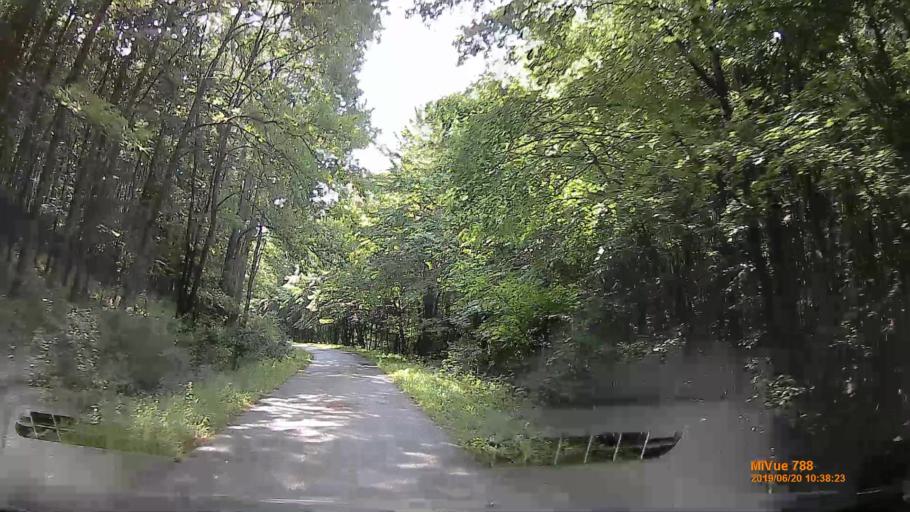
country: HU
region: Baranya
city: Hidas
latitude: 46.2004
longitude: 18.5366
